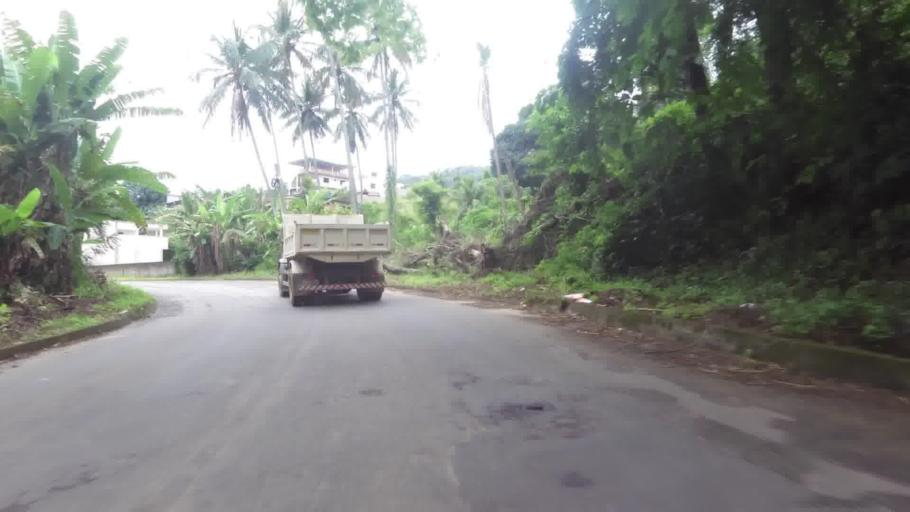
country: BR
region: Espirito Santo
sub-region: Iconha
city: Iconha
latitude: -20.7756
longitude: -40.8270
